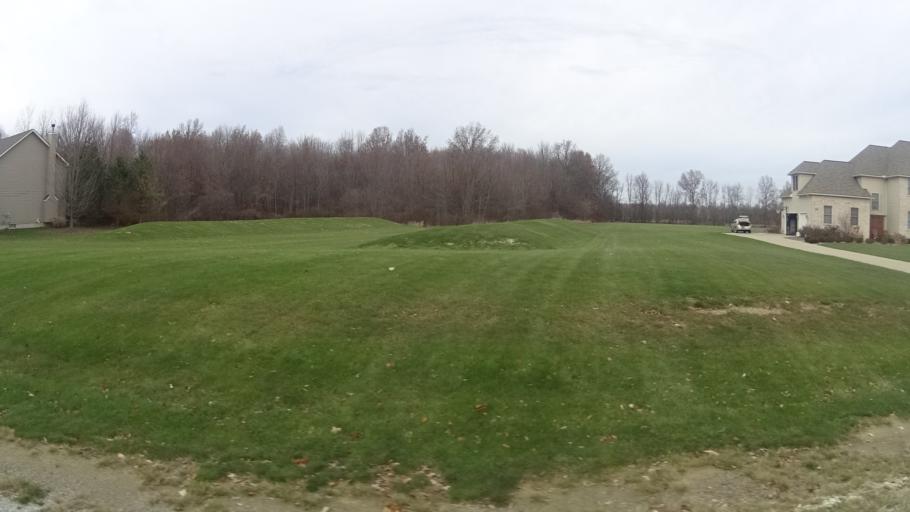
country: US
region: Ohio
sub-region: Lorain County
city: Eaton Estates
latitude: 41.2797
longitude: -81.9606
